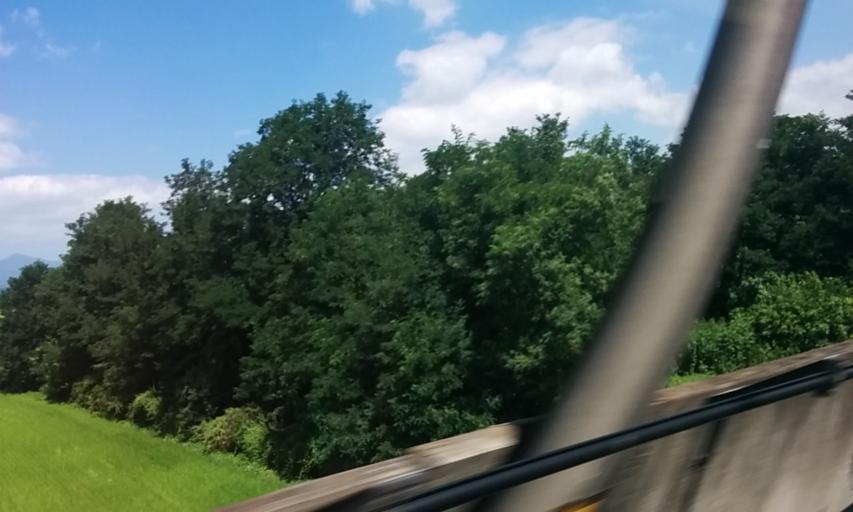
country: JP
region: Fukushima
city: Sukagawa
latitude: 37.2563
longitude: 140.3066
